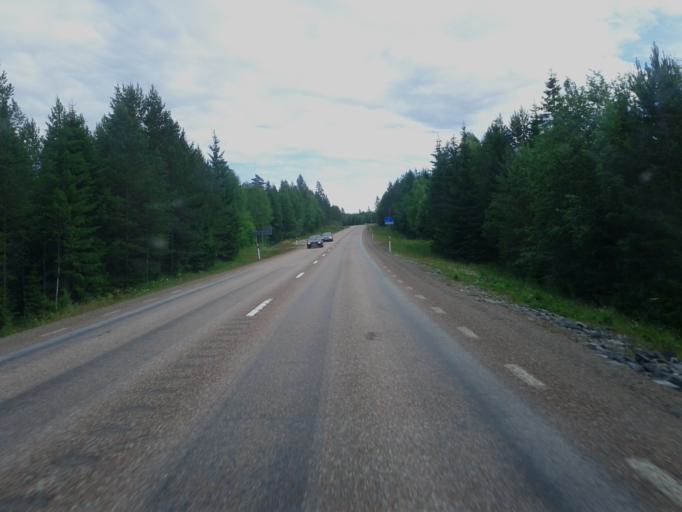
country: SE
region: Dalarna
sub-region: Faluns Kommun
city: Bjursas
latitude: 60.7925
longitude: 15.2773
